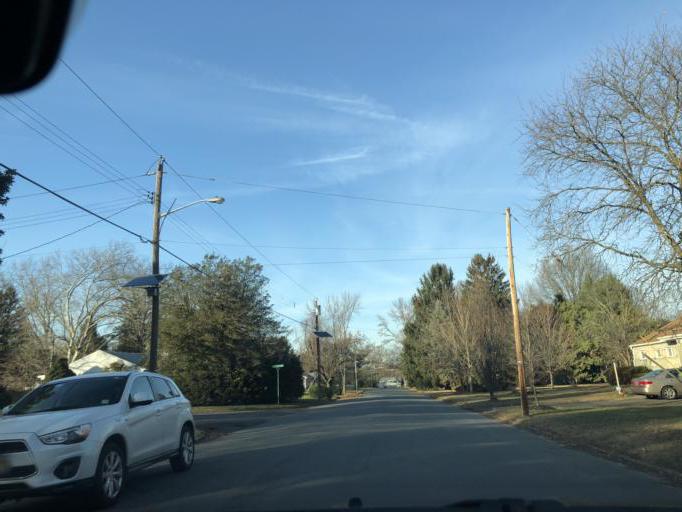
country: US
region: New Jersey
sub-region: Burlington County
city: Moorestown-Lenola
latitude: 39.9594
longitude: -74.9702
